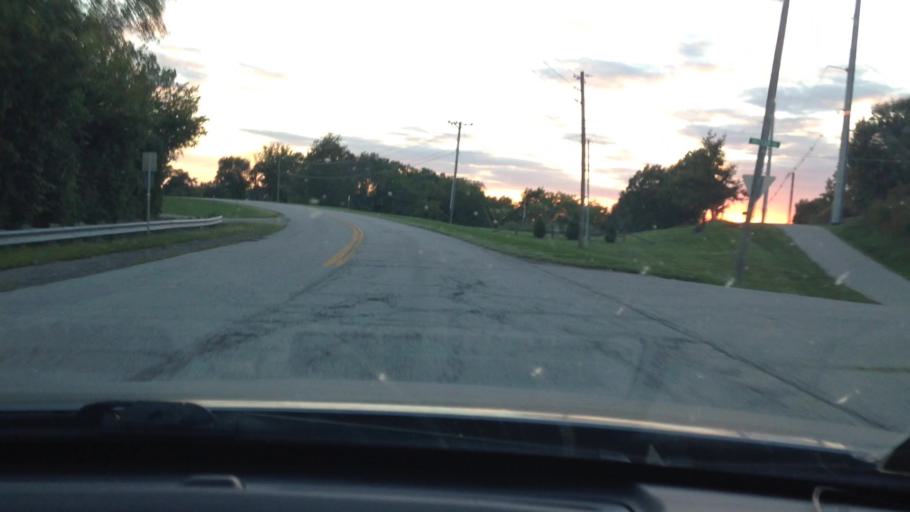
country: US
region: Kansas
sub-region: Leavenworth County
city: Lansing
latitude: 39.1867
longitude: -94.8234
